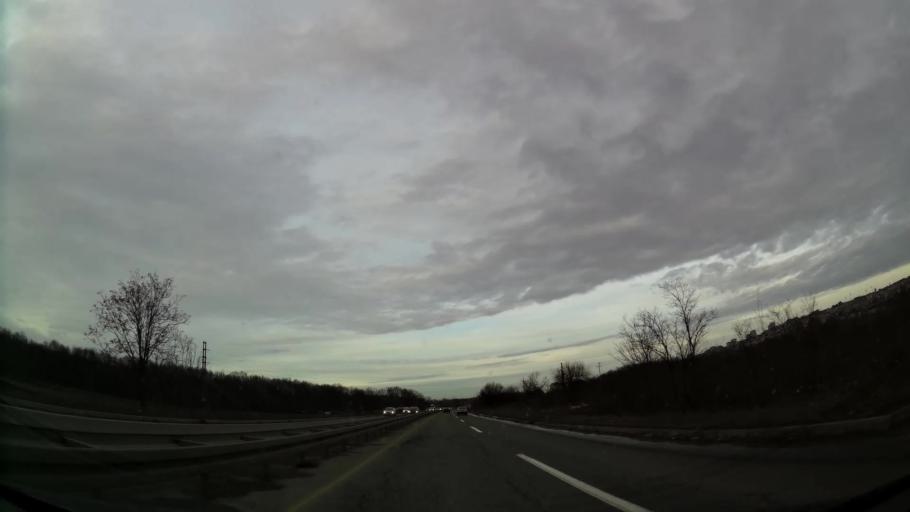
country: RS
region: Central Serbia
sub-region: Belgrade
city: Cukarica
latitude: 44.7722
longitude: 20.3960
